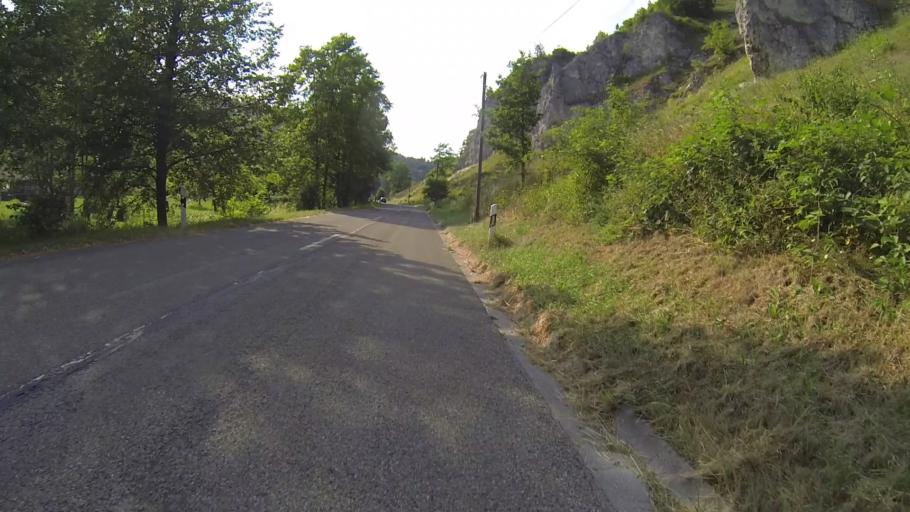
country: DE
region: Baden-Wuerttemberg
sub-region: Tuebingen Region
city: Dornstadt
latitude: 48.4442
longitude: 9.8679
